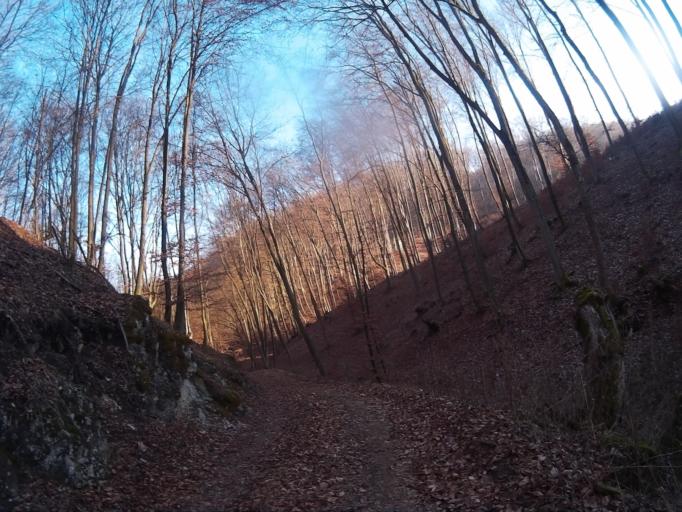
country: HU
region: Borsod-Abauj-Zemplen
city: Rudabanya
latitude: 48.5232
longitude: 20.6052
